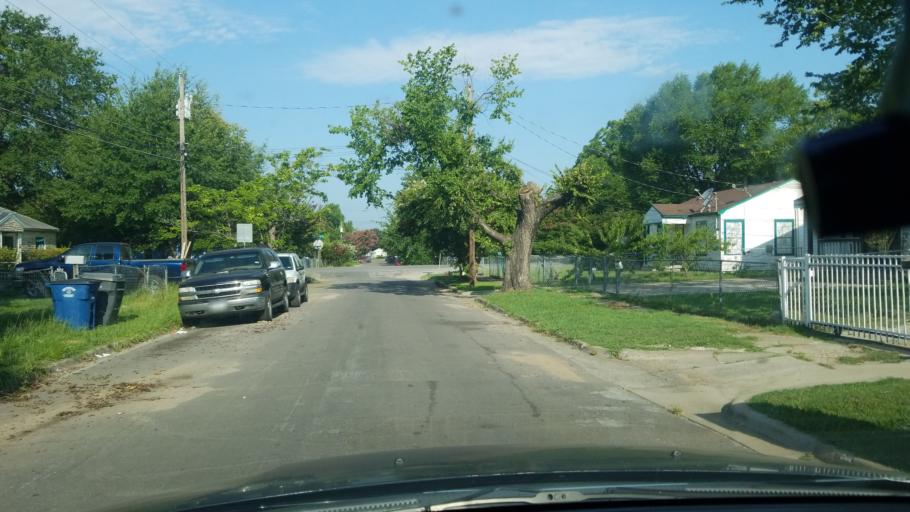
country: US
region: Texas
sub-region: Dallas County
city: Balch Springs
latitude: 32.7227
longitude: -96.6877
